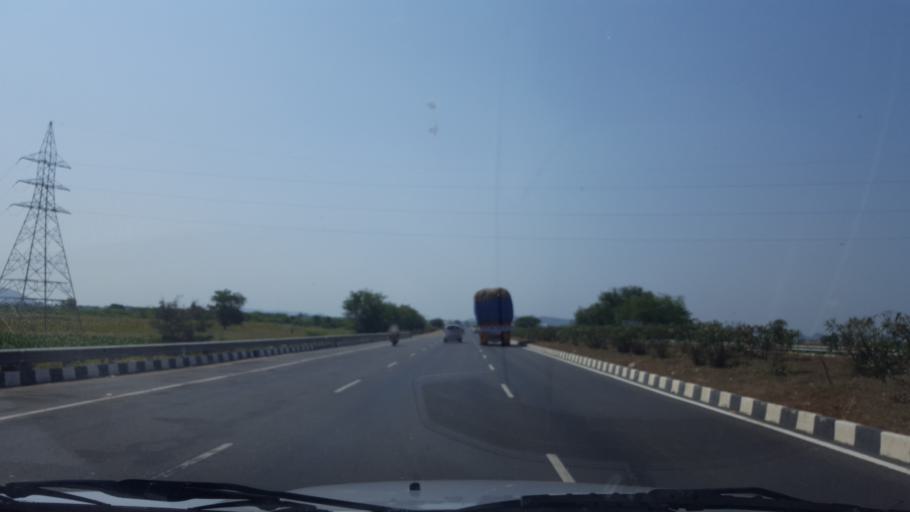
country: IN
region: Andhra Pradesh
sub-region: Guntur
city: Chilakalurupet
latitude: 16.0240
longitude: 80.1257
